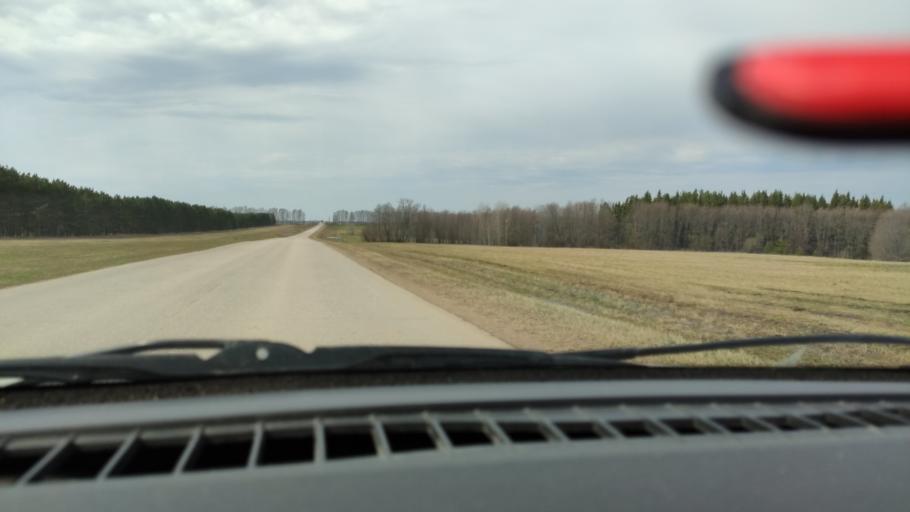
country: RU
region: Bashkortostan
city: Dyurtyuli
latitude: 55.6640
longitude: 55.0697
